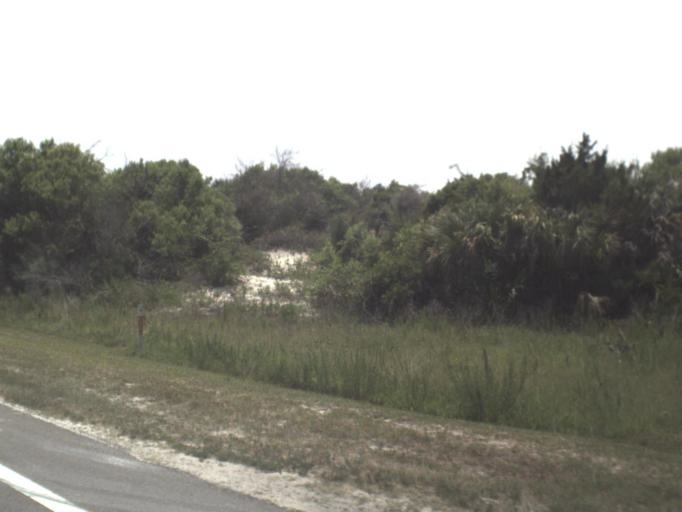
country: US
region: Florida
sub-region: Duval County
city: Atlantic Beach
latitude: 30.4455
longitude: -81.4157
